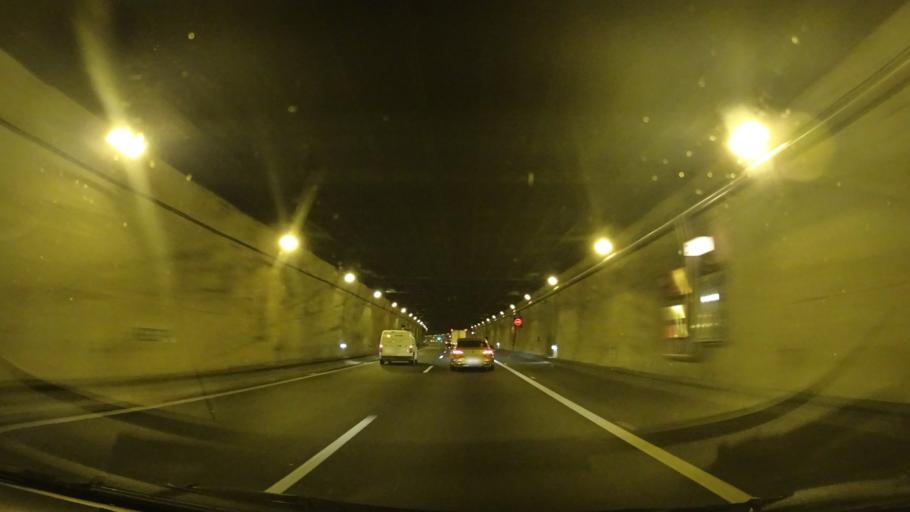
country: ES
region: Madrid
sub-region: Provincia de Madrid
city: Guadarrama
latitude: 40.7104
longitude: -4.1399
